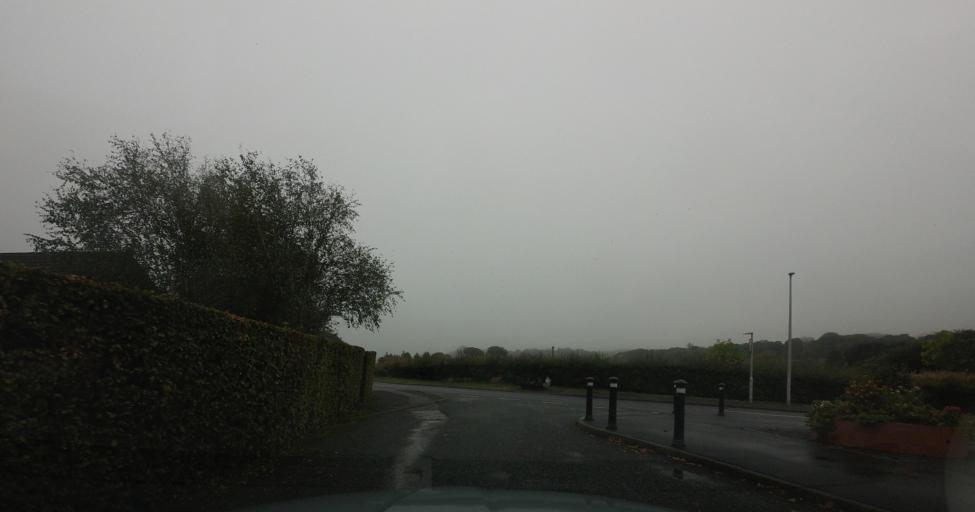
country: GB
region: Scotland
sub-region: Aberdeenshire
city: Oldmeldrum
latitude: 57.4307
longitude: -2.3942
